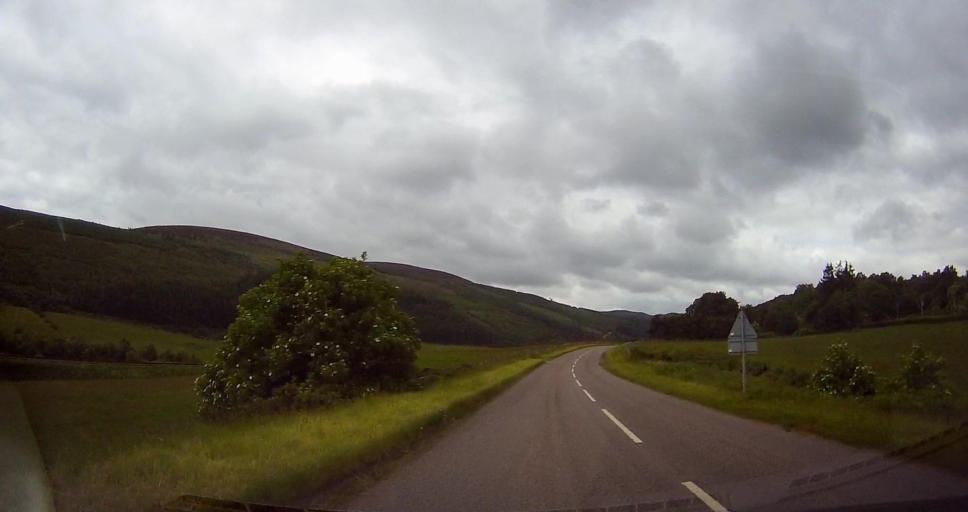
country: GB
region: Scotland
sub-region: Highland
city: Dornoch
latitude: 57.9832
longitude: -4.1421
